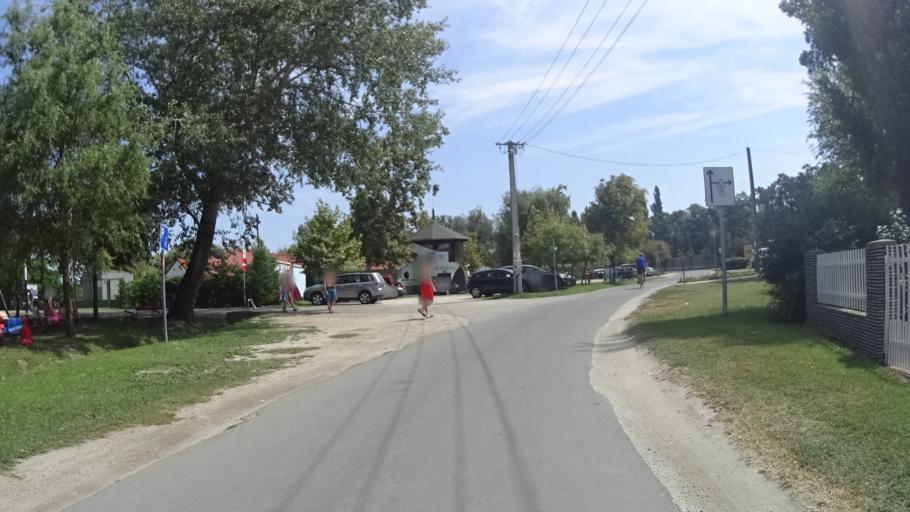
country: HU
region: Somogy
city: Balatonfenyves
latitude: 46.7087
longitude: 17.4536
